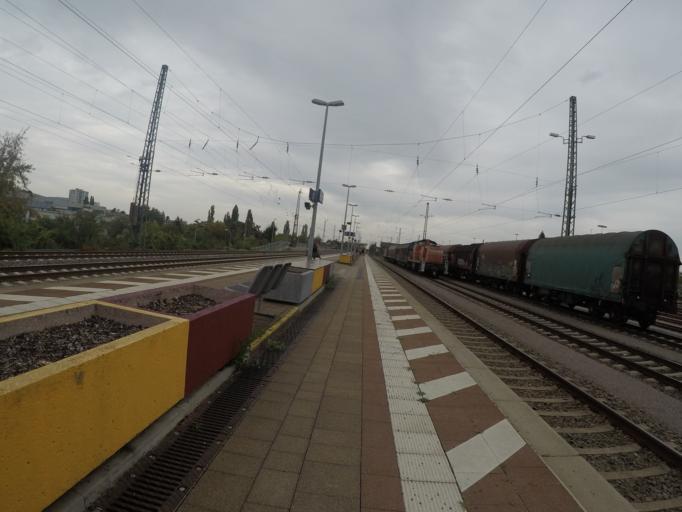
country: DE
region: Rheinland-Pfalz
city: Neustadt
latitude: 49.3529
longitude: 8.1565
